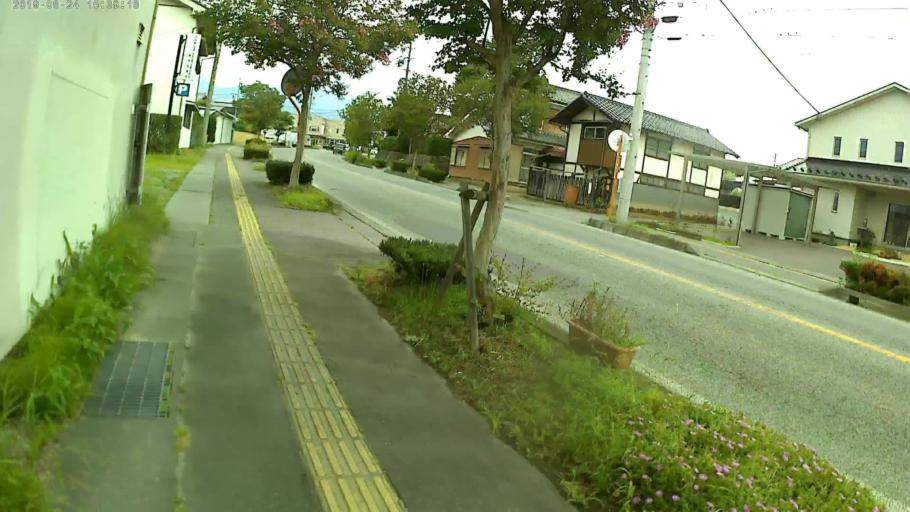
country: JP
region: Nagano
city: Komoro
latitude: 36.2781
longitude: 138.4783
